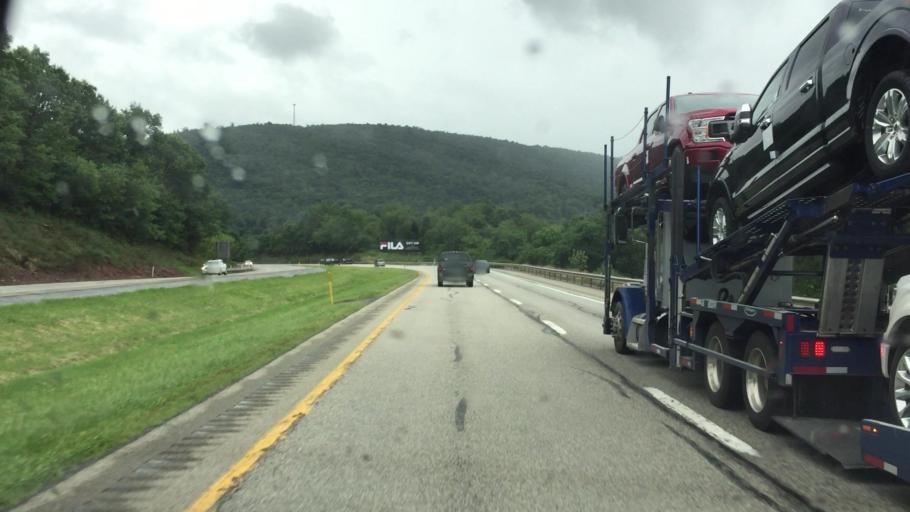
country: US
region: Pennsylvania
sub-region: Bedford County
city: Earlston
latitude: 39.9600
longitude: -78.2470
